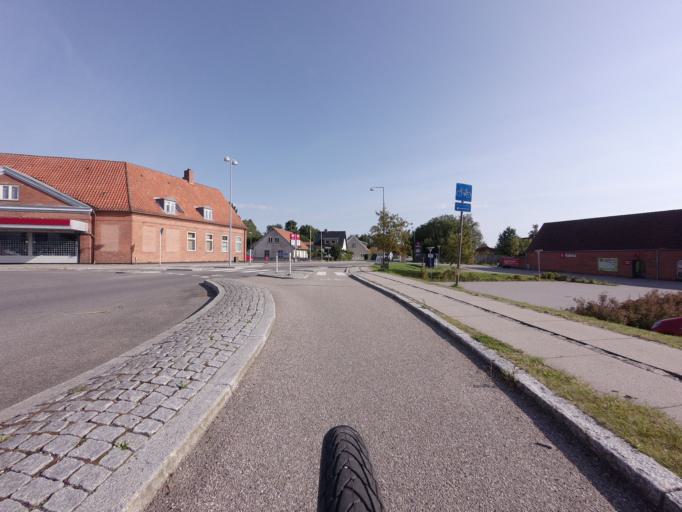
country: DK
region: Zealand
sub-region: Soro Kommune
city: Soro
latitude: 55.4537
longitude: 11.5581
